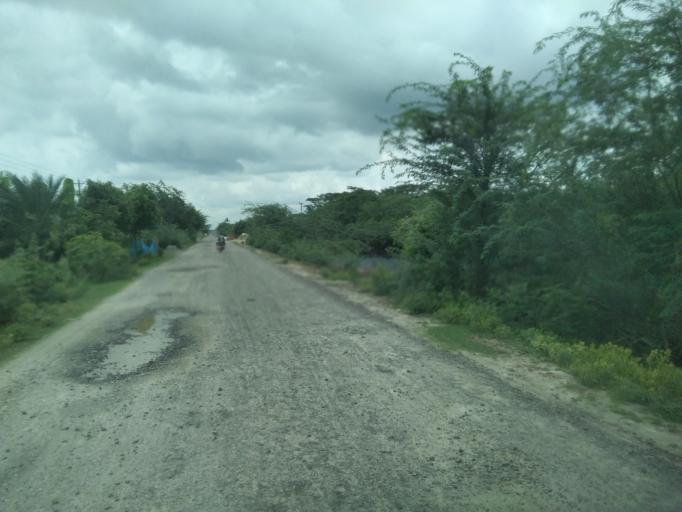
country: IN
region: West Bengal
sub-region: North 24 Parganas
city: Gosaba
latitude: 22.2665
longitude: 89.1740
